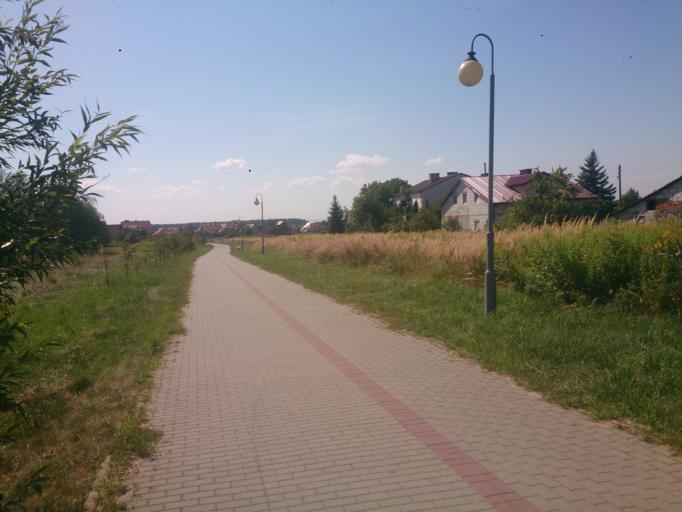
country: PL
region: Subcarpathian Voivodeship
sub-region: Powiat rzeszowski
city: Glogow Malopolski
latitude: 50.1480
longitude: 21.9664
